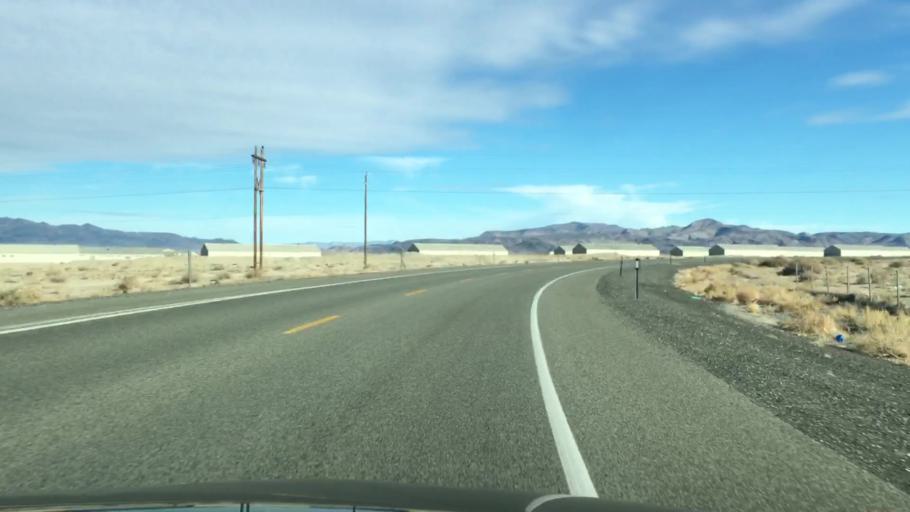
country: US
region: Nevada
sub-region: Mineral County
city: Hawthorne
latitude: 38.5335
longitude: -118.6145
